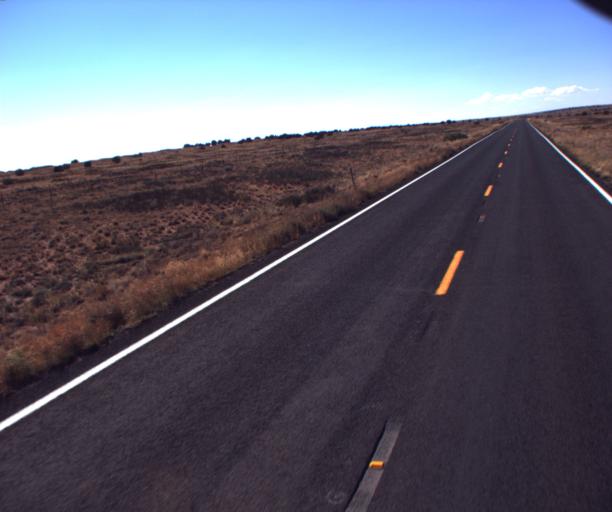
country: US
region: Arizona
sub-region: Coconino County
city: Tuba City
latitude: 35.9118
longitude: -110.8686
